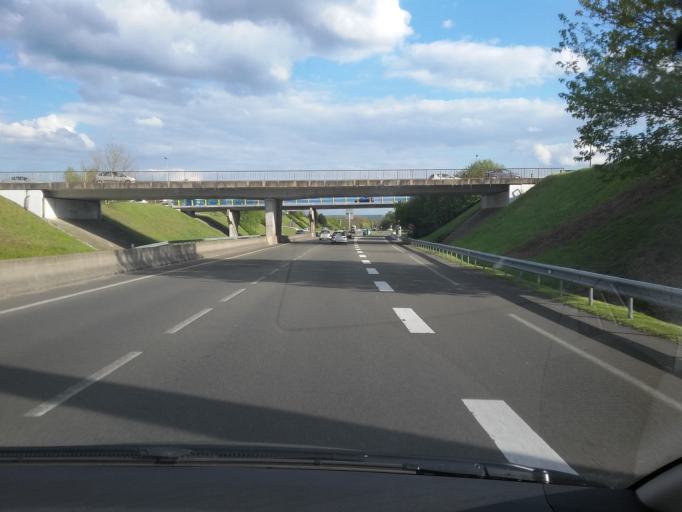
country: FR
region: Picardie
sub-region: Departement de l'Oise
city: Jaux
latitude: 49.4054
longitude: 2.7804
